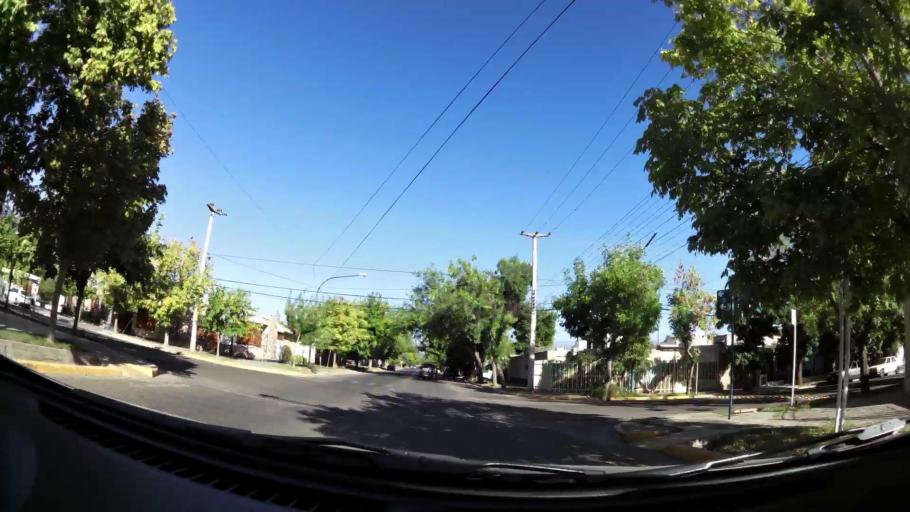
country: AR
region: Mendoza
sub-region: Departamento de Godoy Cruz
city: Godoy Cruz
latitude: -32.9310
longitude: -68.8337
